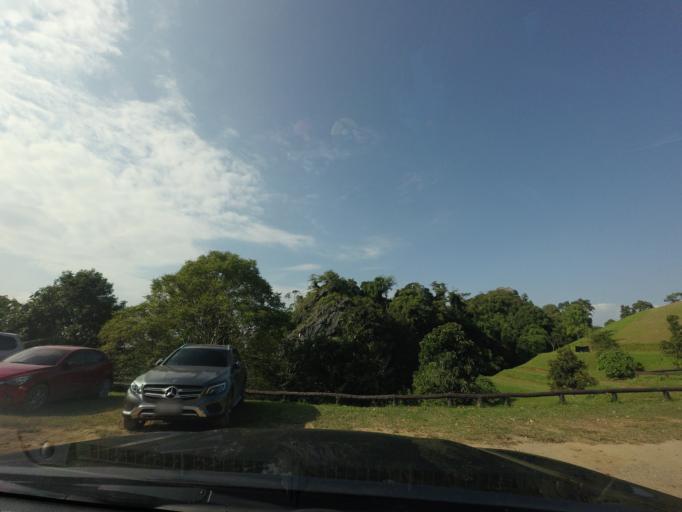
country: TH
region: Nan
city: Na Noi
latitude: 18.3750
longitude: 100.8262
